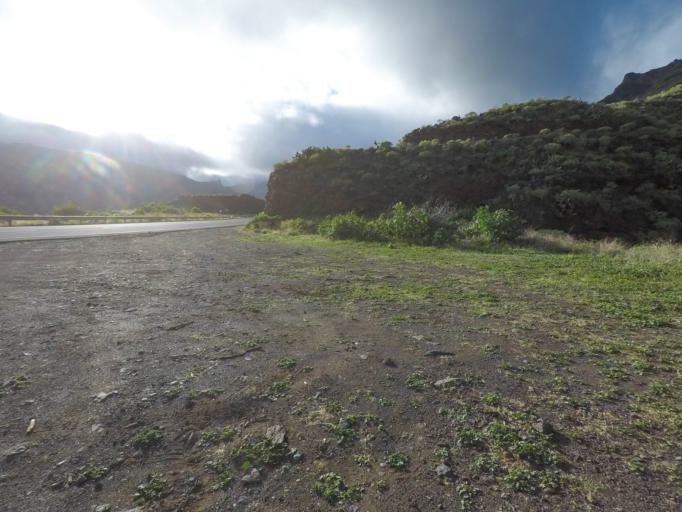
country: ES
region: Canary Islands
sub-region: Provincia de Santa Cruz de Tenerife
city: San Sebastian de la Gomera
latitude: 28.1239
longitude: -17.1575
